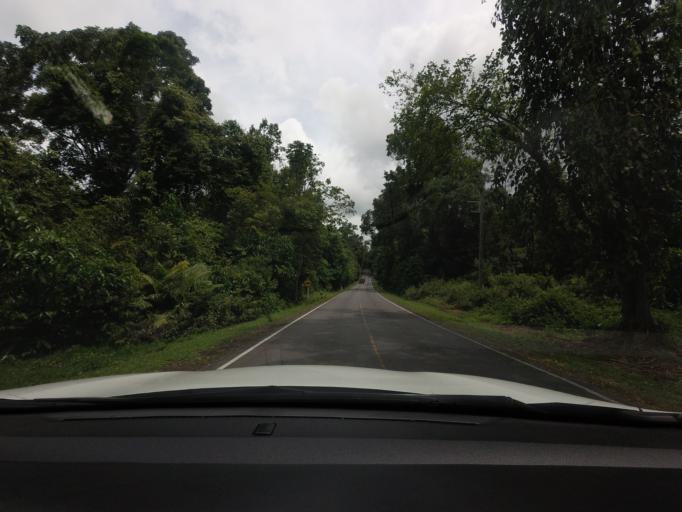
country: TH
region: Nakhon Ratchasima
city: Pak Chong
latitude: 14.4438
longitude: 101.3690
